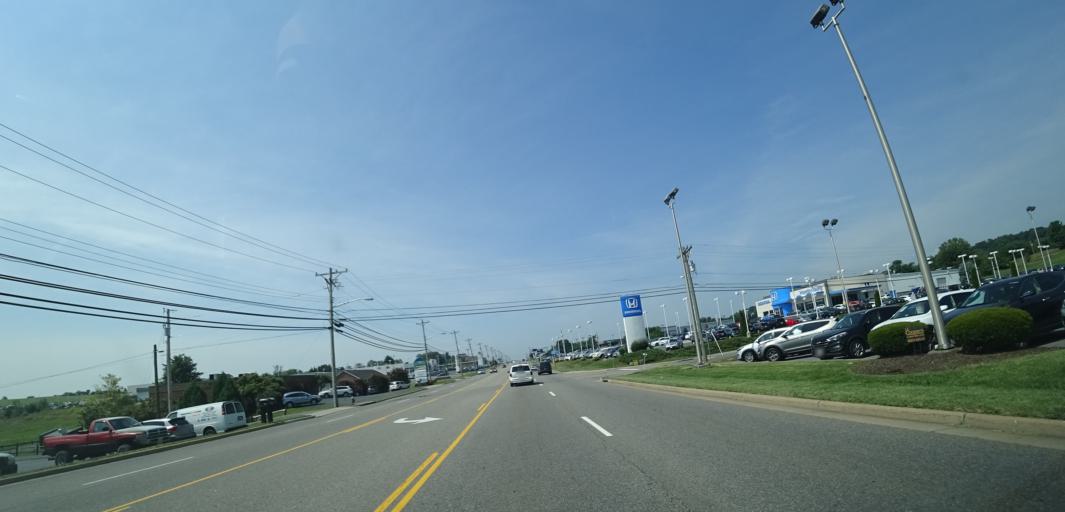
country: US
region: Virginia
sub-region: Rockingham County
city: Dayton
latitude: 38.4161
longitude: -78.8981
